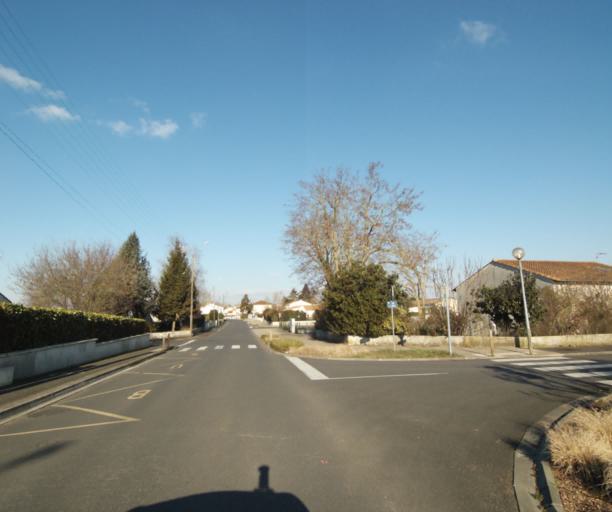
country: FR
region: Poitou-Charentes
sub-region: Departement des Deux-Sevres
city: Niort
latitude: 46.3428
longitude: -0.4595
